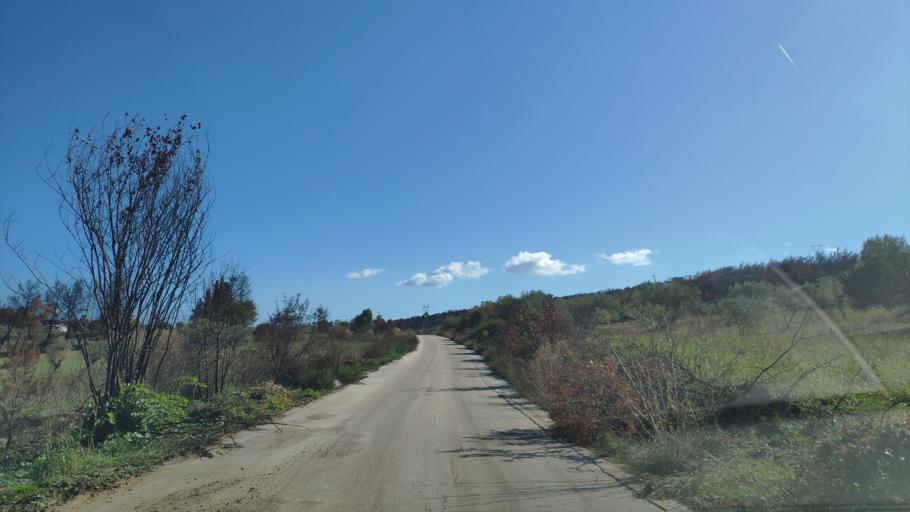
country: GR
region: Peloponnese
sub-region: Nomos Korinthias
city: Athikia
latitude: 37.8452
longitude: 22.9351
